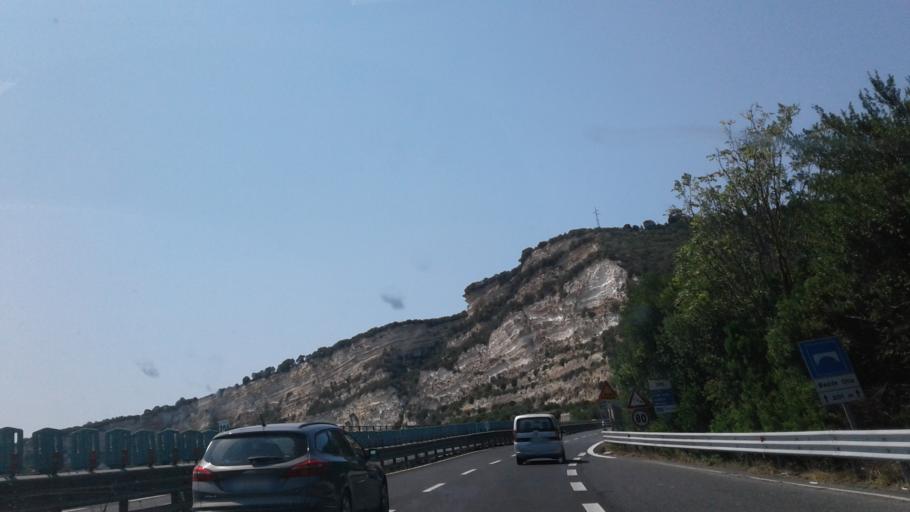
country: IT
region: Sardinia
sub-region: Provincia di Sassari
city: Ossi
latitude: 40.6993
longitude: 8.5932
